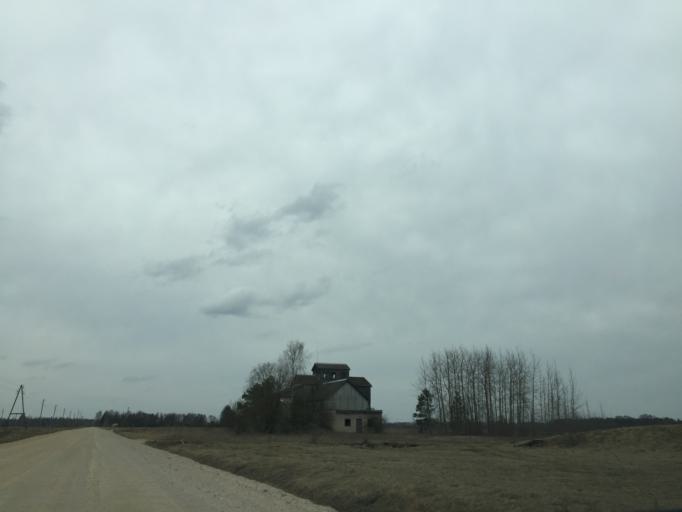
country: LV
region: Livani
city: Livani
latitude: 56.3374
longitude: 26.1600
